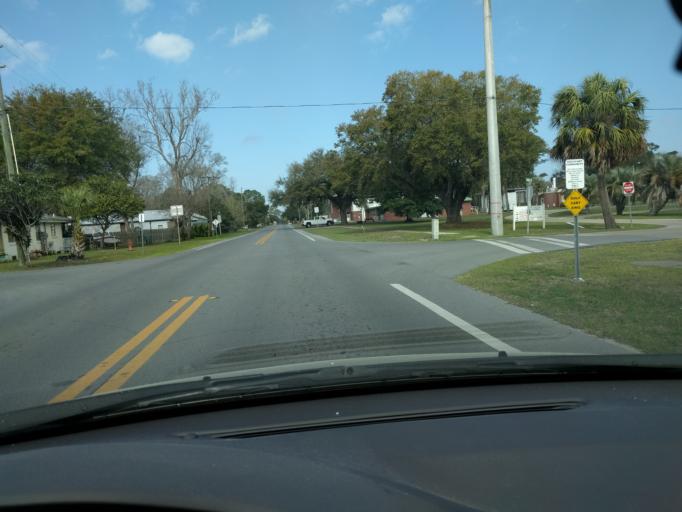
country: US
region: Florida
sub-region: Franklin County
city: Apalachicola
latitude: 29.7233
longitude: -84.9923
